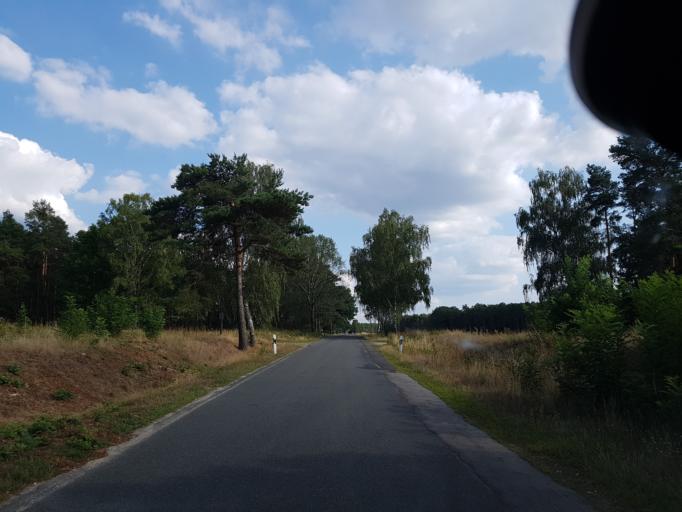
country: DE
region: Brandenburg
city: Bronkow
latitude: 51.6963
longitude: 13.8794
